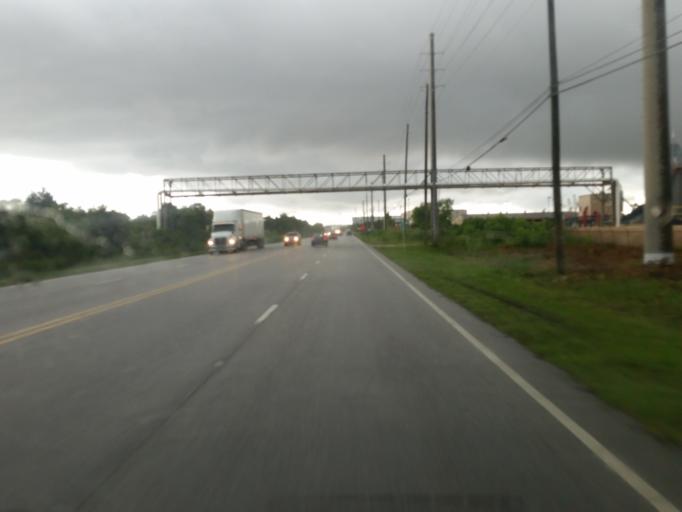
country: US
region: Alabama
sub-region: Mobile County
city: Mobile
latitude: 30.7088
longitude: -88.0333
